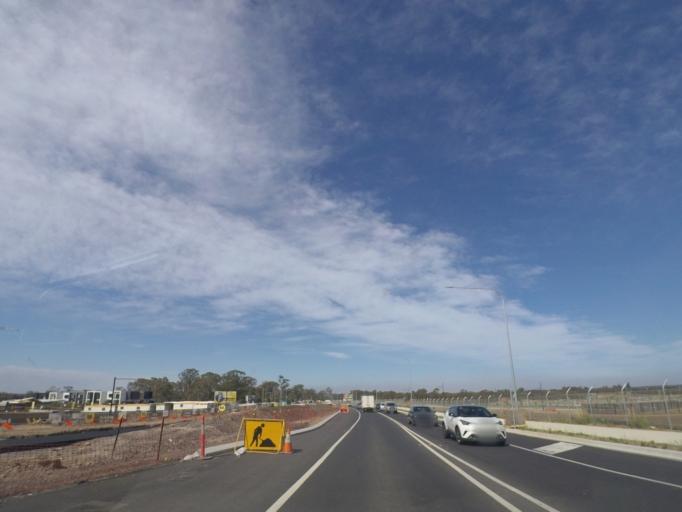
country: AU
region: New South Wales
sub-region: Campbelltown Municipality
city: Denham Court
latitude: -33.9744
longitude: 150.8578
